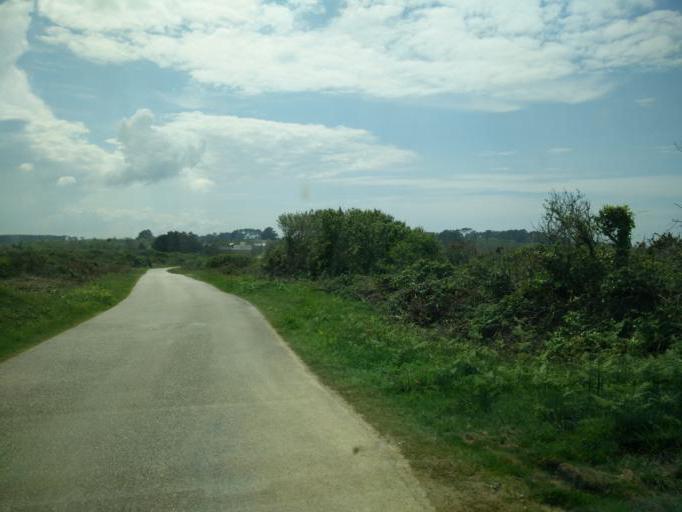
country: FR
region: Brittany
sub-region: Departement du Finistere
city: Roscanvel
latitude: 48.3285
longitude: -4.5688
